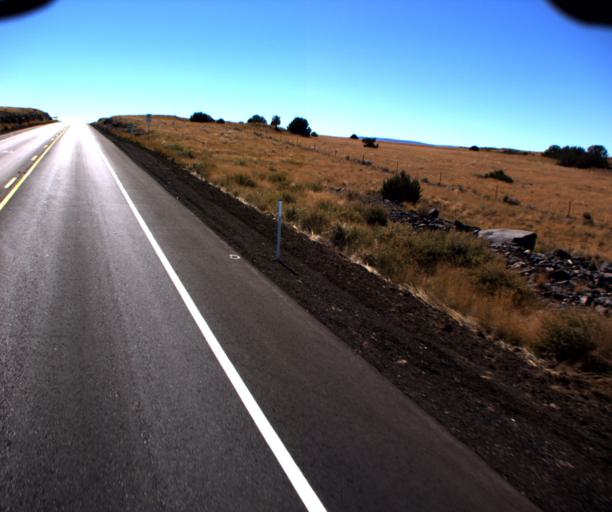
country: US
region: Arizona
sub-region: Apache County
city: Springerville
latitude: 34.2472
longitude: -109.3494
